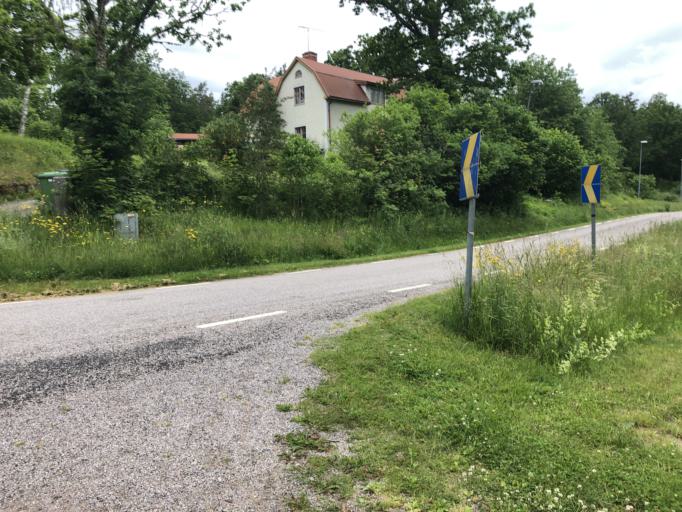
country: SE
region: Kalmar
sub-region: Vasterviks Kommun
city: Ankarsrum
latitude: 57.5248
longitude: 16.4711
